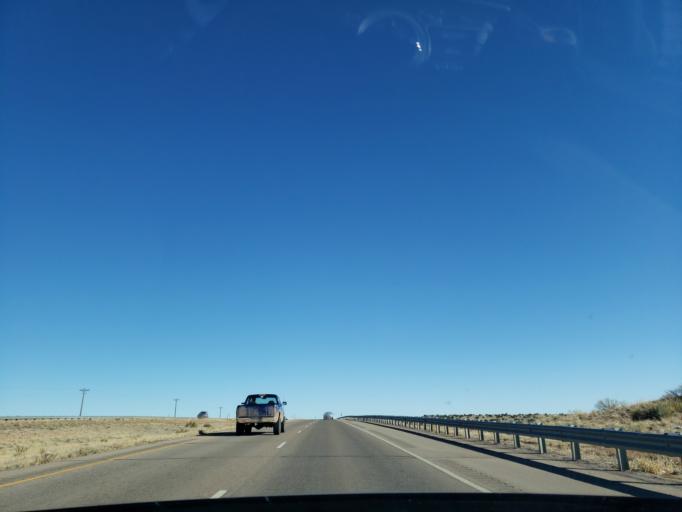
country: US
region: Colorado
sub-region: Fremont County
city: Florence
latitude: 38.4317
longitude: -105.0925
